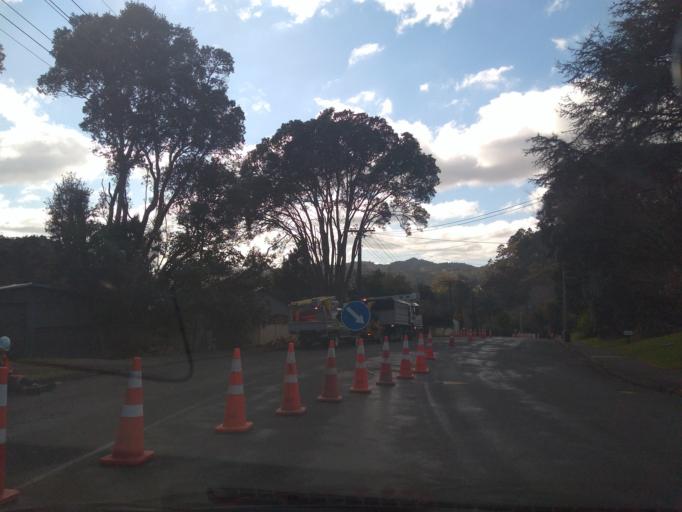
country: NZ
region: Northland
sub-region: Whangarei
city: Whangarei
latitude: -35.7029
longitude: 174.3277
